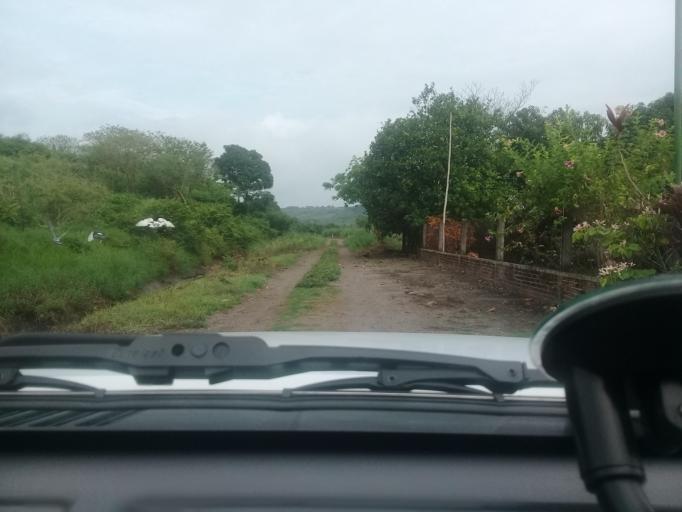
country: MX
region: Veracruz
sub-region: Paso de Ovejas
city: Tolome
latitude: 19.2621
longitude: -96.4135
